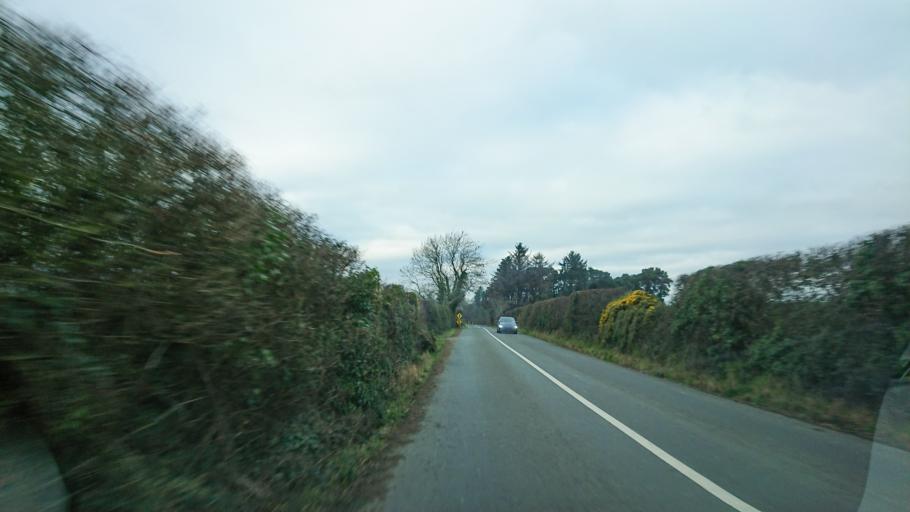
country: IE
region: Munster
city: Carrick-on-Suir
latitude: 52.2984
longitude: -7.4764
